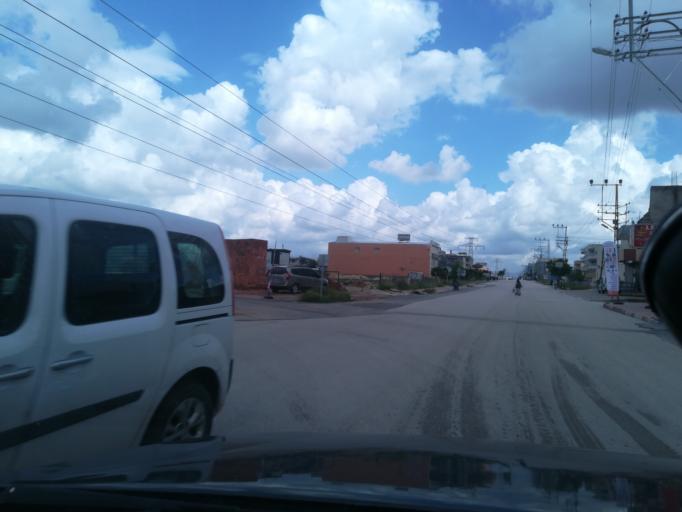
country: TR
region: Adana
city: Yuregir
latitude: 36.9760
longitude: 35.3895
